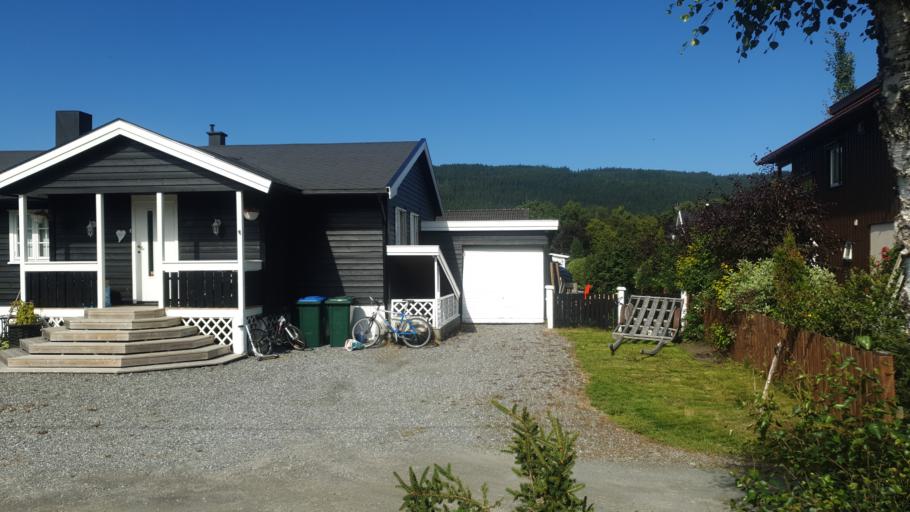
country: NO
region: Sor-Trondelag
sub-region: Orkdal
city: Orkanger
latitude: 63.2807
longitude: 9.8317
